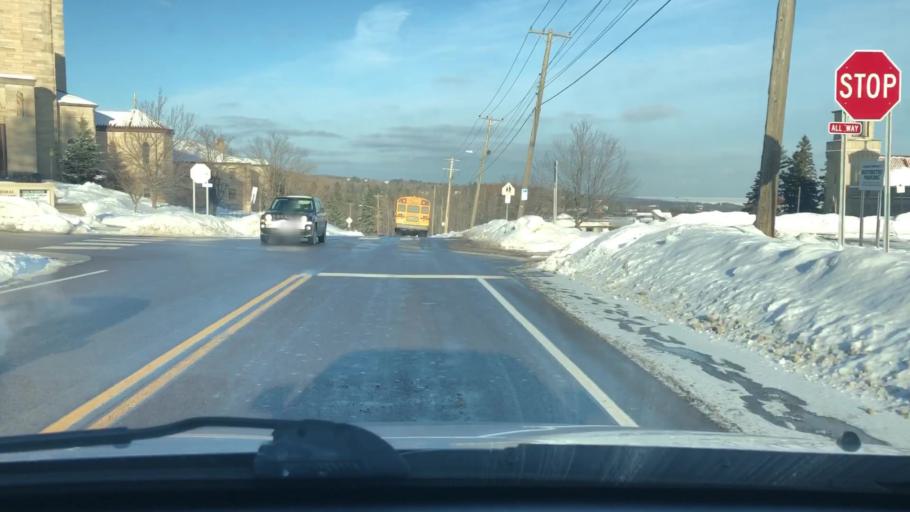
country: US
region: Minnesota
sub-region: Saint Louis County
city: Duluth
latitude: 46.8157
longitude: -92.0685
